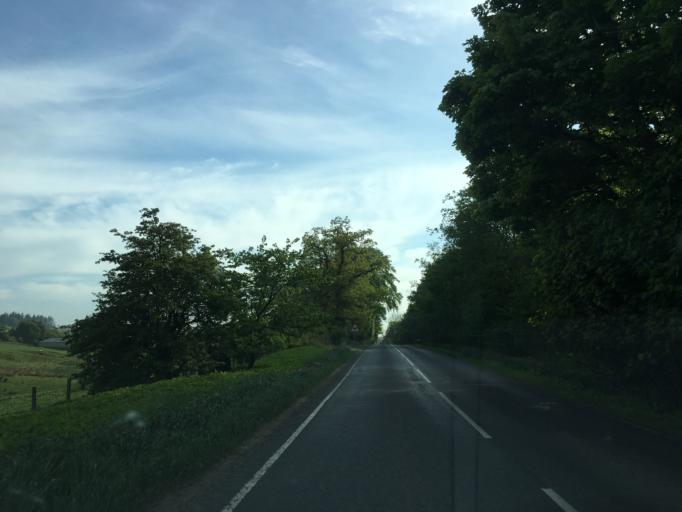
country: GB
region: Scotland
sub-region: Midlothian
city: Penicuik
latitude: 55.7684
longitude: -3.2505
